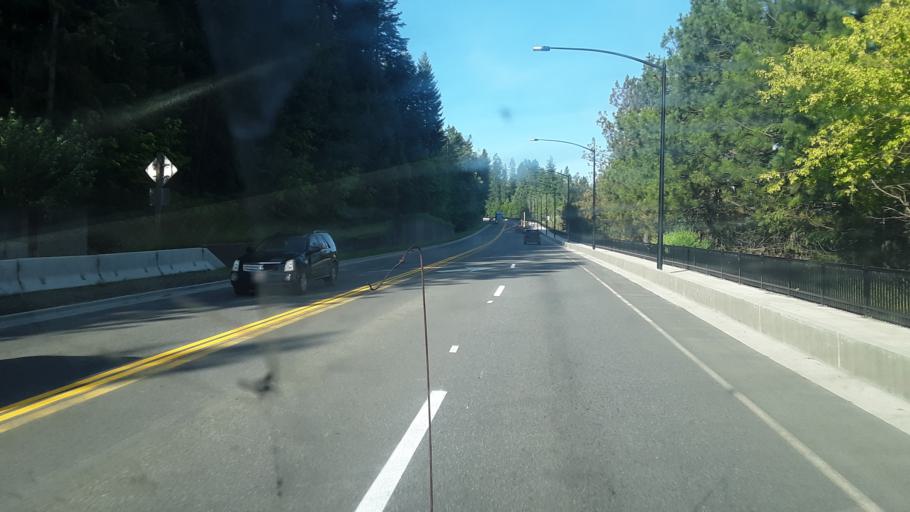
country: US
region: Idaho
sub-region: Boundary County
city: Bonners Ferry
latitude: 48.6948
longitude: -116.3124
